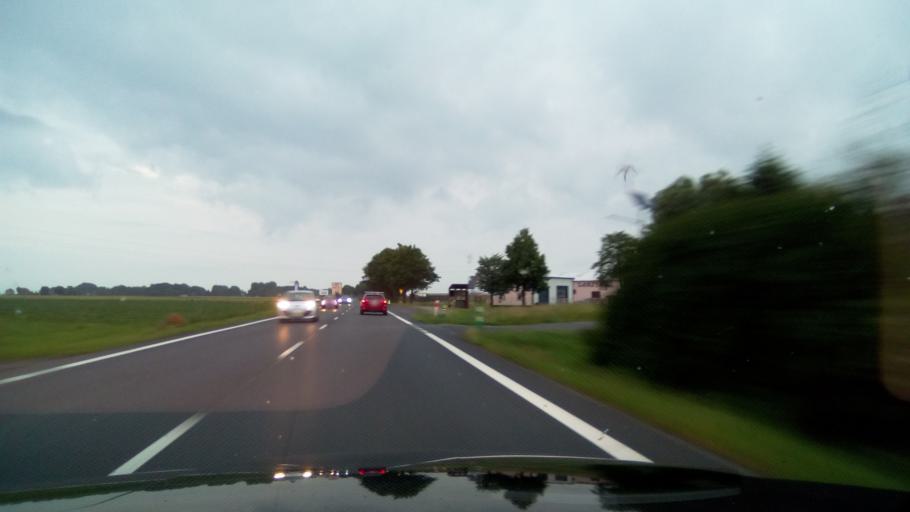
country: PL
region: Greater Poland Voivodeship
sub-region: Powiat poznanski
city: Pobiedziska
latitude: 52.4950
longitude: 17.3325
